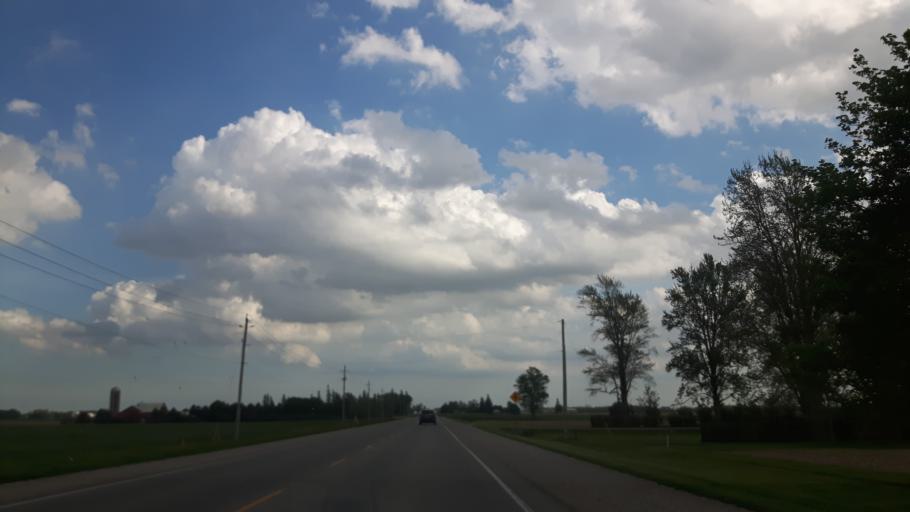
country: CA
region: Ontario
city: South Huron
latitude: 43.3827
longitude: -81.4880
